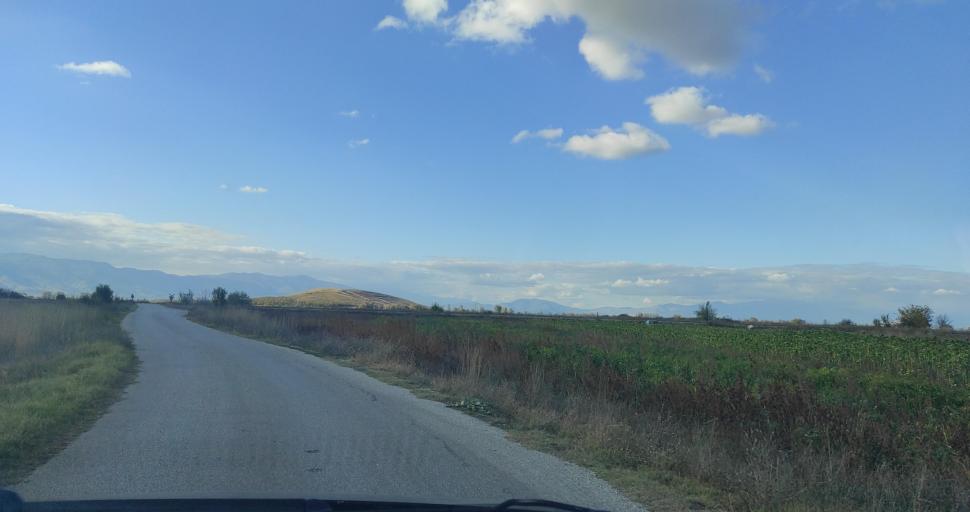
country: MK
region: Prilep
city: Topolcani
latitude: 41.2770
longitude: 21.4322
